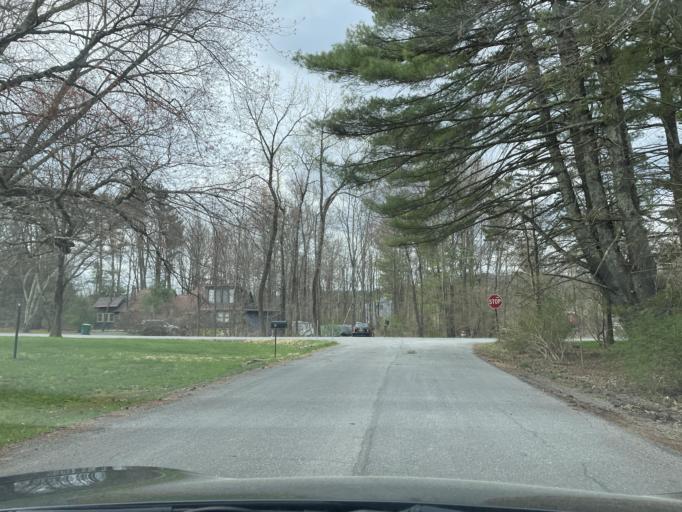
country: US
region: New York
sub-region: Ulster County
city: Woodstock
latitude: 42.0388
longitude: -74.1092
